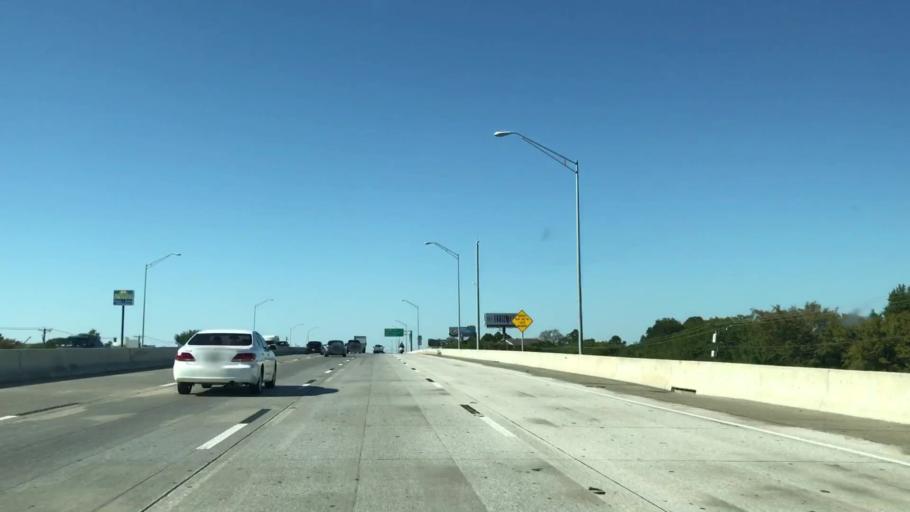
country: US
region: Texas
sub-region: Denton County
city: Hickory Creek
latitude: 33.1398
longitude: -97.0491
